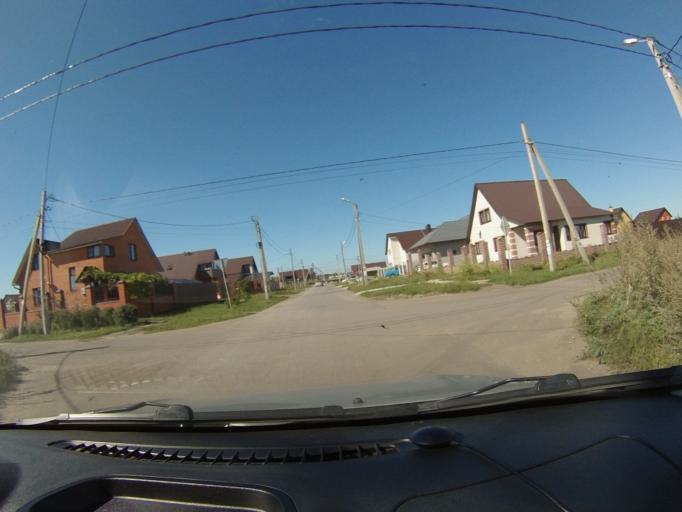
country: RU
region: Tambov
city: Tambov
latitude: 52.7762
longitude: 41.3726
